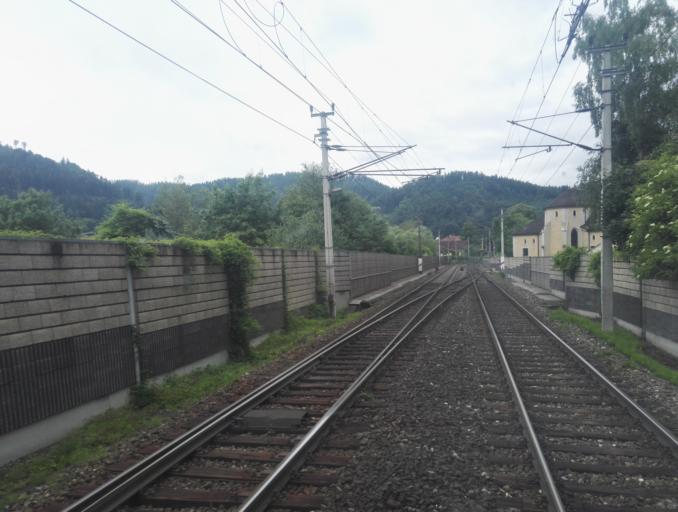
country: AT
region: Styria
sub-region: Politischer Bezirk Bruck-Muerzzuschlag
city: Kapfenberg
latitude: 47.4412
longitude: 15.2871
